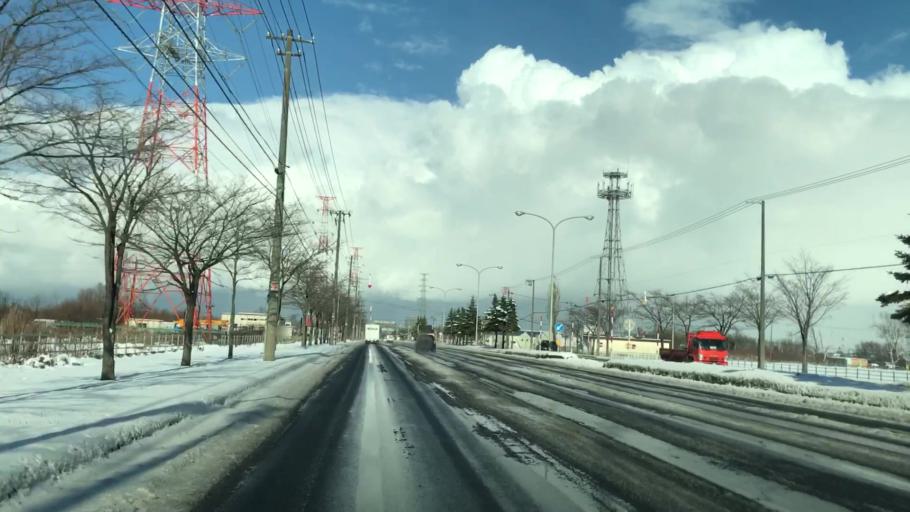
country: JP
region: Hokkaido
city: Sapporo
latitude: 43.1356
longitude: 141.4152
